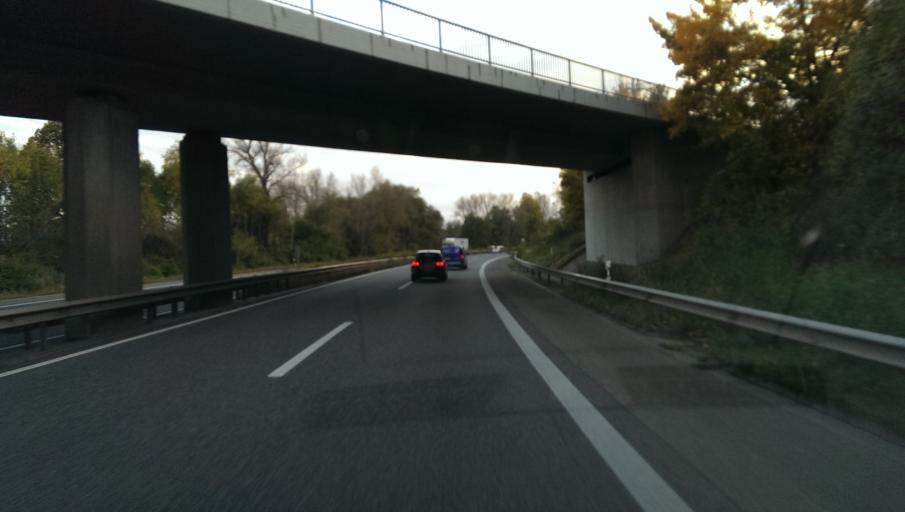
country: DE
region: Rheinland-Pfalz
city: Germersheim
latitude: 49.2303
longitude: 8.3578
